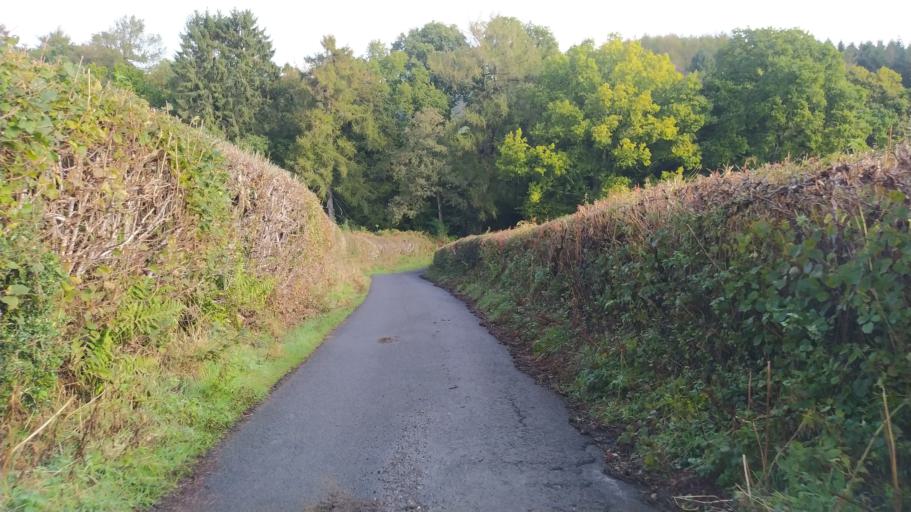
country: GB
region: England
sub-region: Dorset
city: Shaftesbury
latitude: 51.0233
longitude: -2.1362
